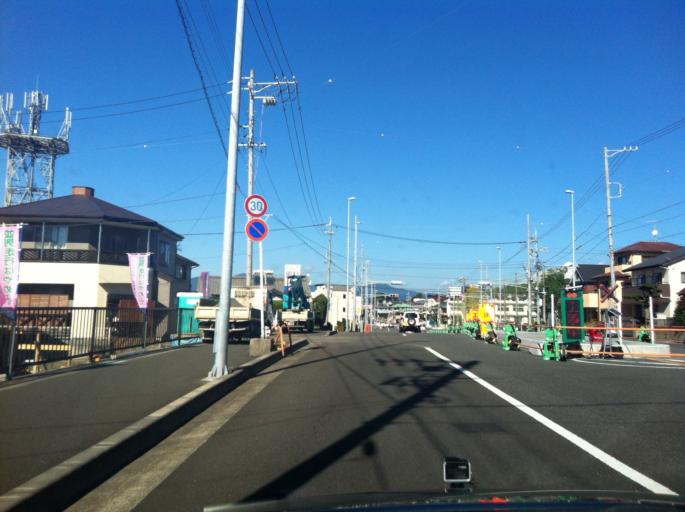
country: JP
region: Shizuoka
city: Shizuoka-shi
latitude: 34.9529
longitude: 138.4285
